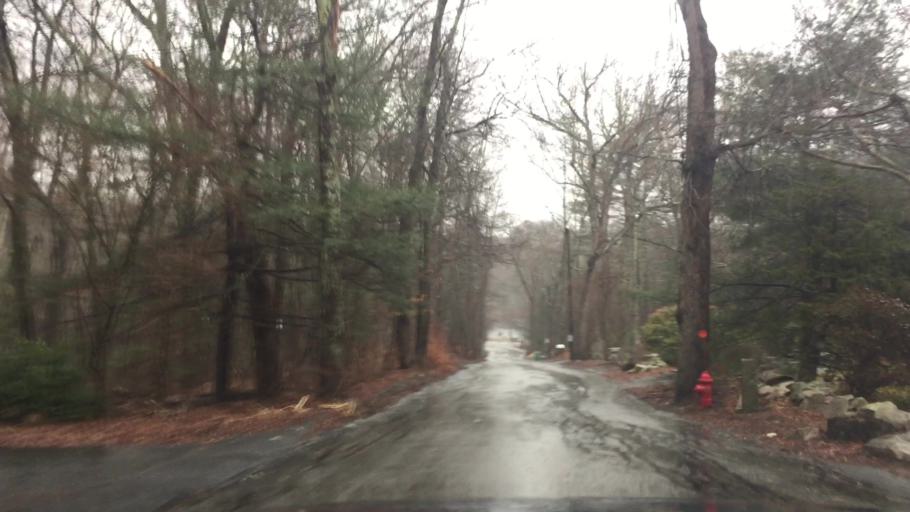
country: US
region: Massachusetts
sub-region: Middlesex County
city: Ashland
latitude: 42.2307
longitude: -71.4671
